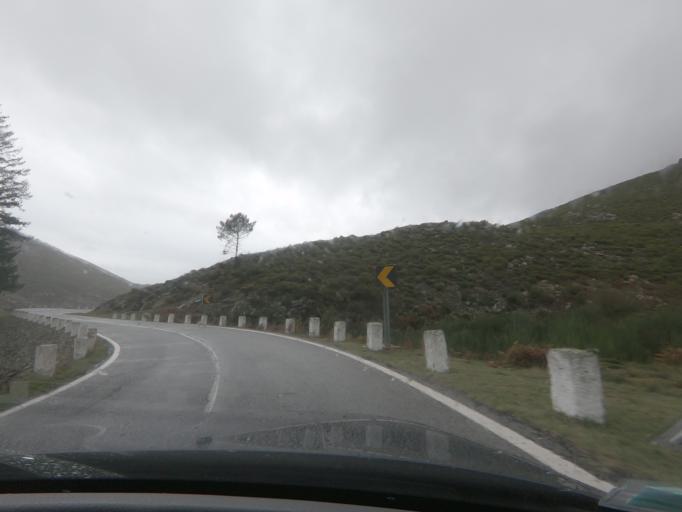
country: PT
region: Vila Real
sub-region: Mondim de Basto
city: Mondim de Basto
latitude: 41.3384
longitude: -7.8648
